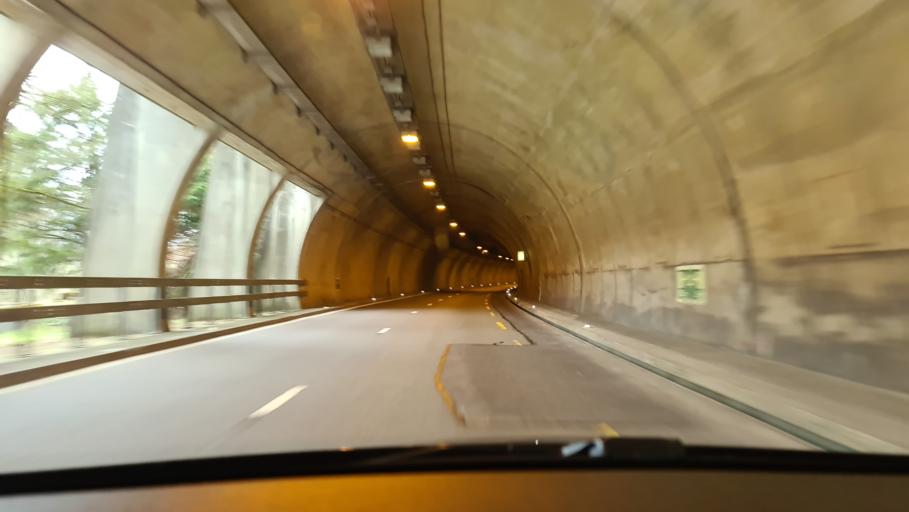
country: CH
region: Bern
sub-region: Jura bernois
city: Pery
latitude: 47.1876
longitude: 7.2358
